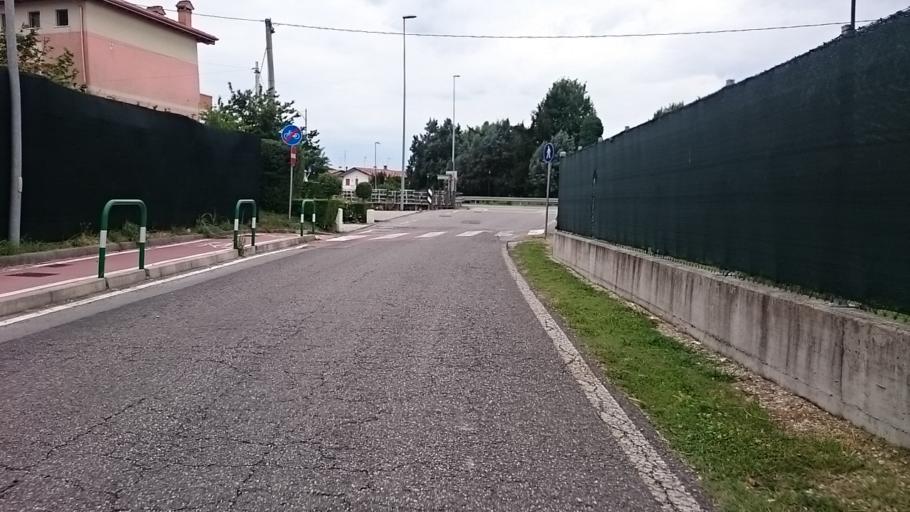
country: IT
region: Veneto
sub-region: Provincia di Padova
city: Bertipaglia
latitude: 45.3170
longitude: 11.8814
